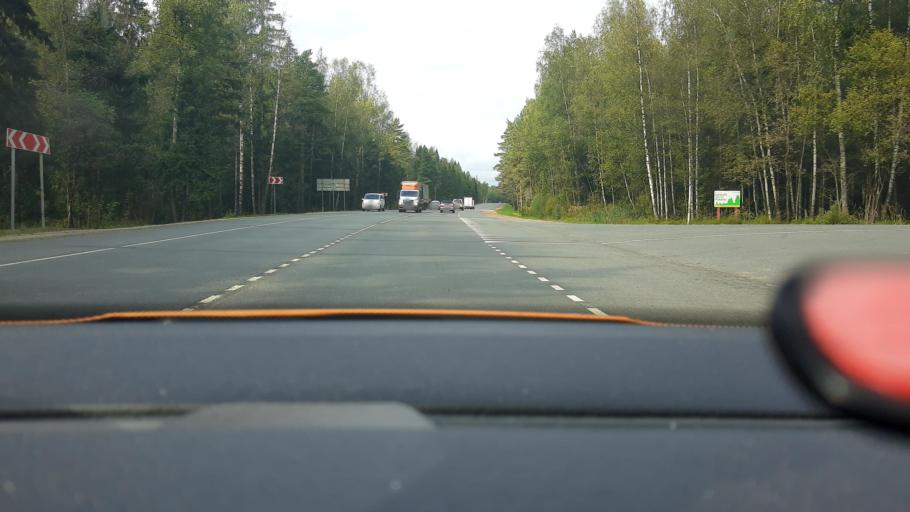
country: RU
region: Moskovskaya
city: Zelenogradskiy
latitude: 56.0839
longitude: 38.0020
